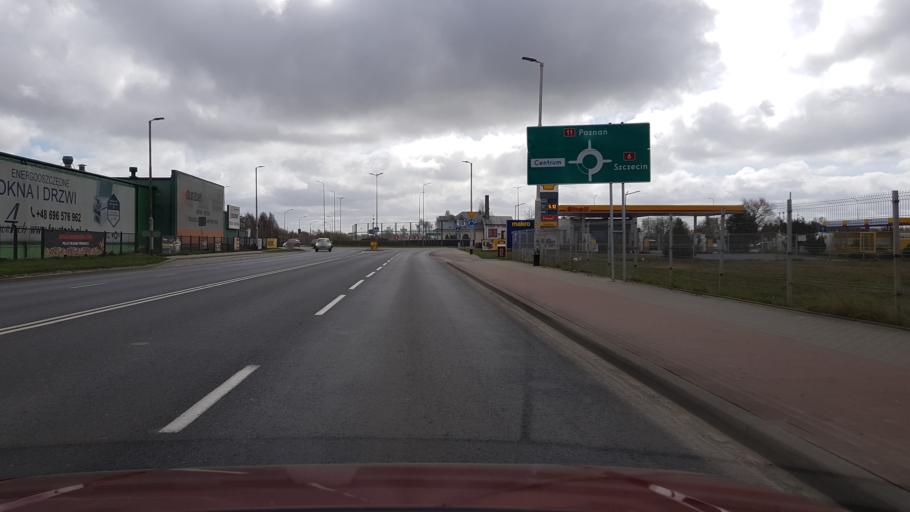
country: PL
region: West Pomeranian Voivodeship
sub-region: Koszalin
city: Koszalin
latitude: 54.1836
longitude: 16.1503
